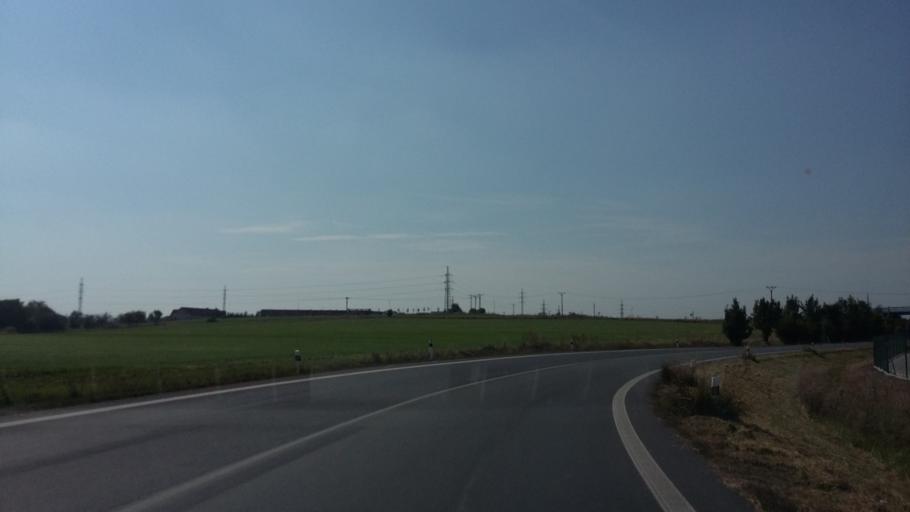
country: CZ
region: Central Bohemia
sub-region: Okres Kolin
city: Kolin
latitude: 50.0589
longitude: 15.2281
